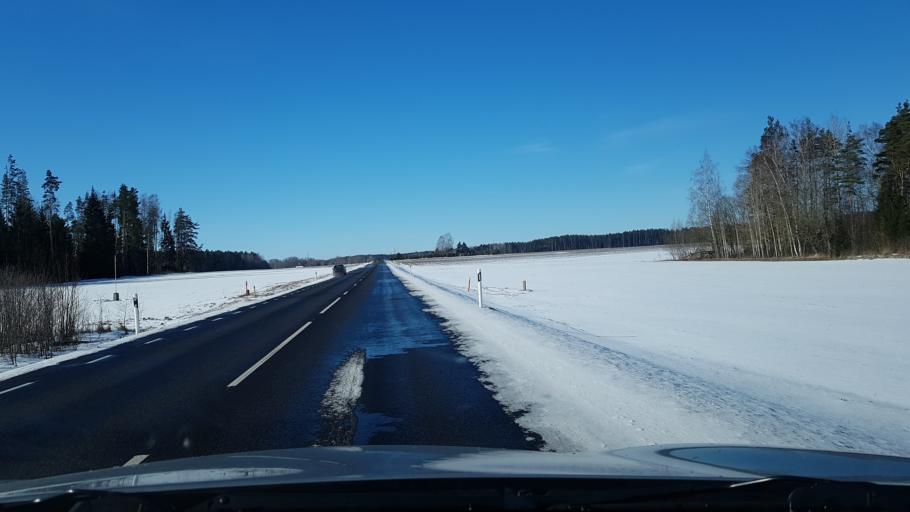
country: EE
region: Polvamaa
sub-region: Polva linn
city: Polva
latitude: 58.0895
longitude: 27.1156
